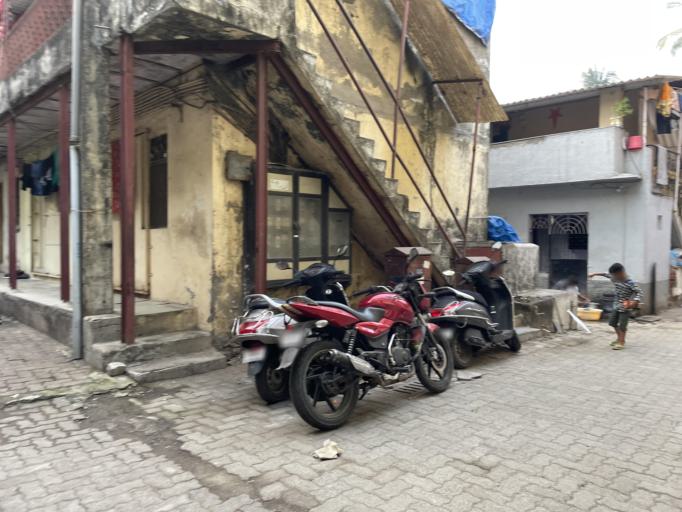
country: IN
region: Maharashtra
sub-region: Mumbai Suburban
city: Borivli
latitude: 19.2378
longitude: 72.8442
